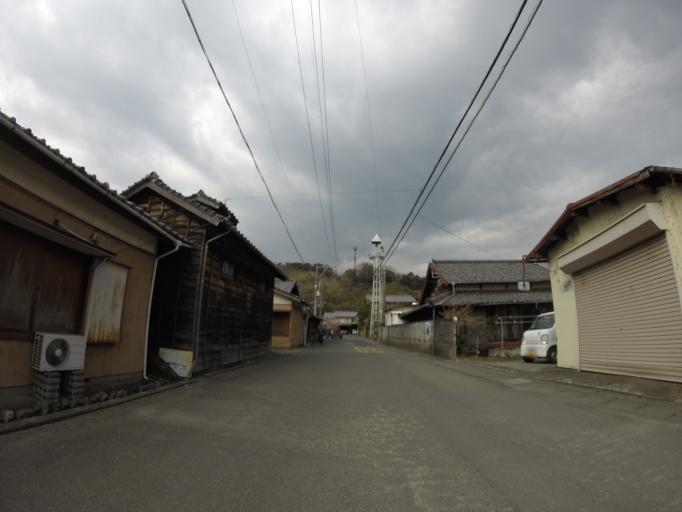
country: JP
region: Shizuoka
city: Shizuoka-shi
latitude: 35.0398
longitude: 138.4483
